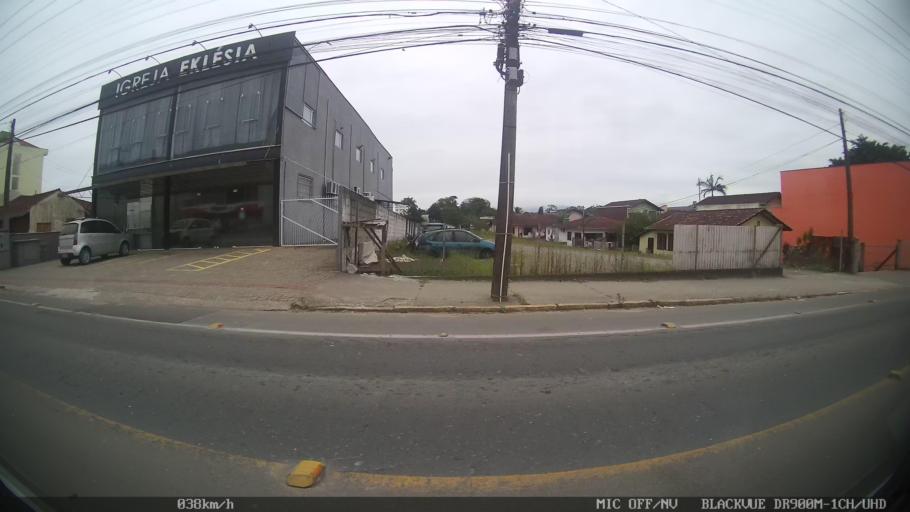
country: BR
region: Santa Catarina
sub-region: Joinville
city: Joinville
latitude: -26.3294
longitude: -48.8379
